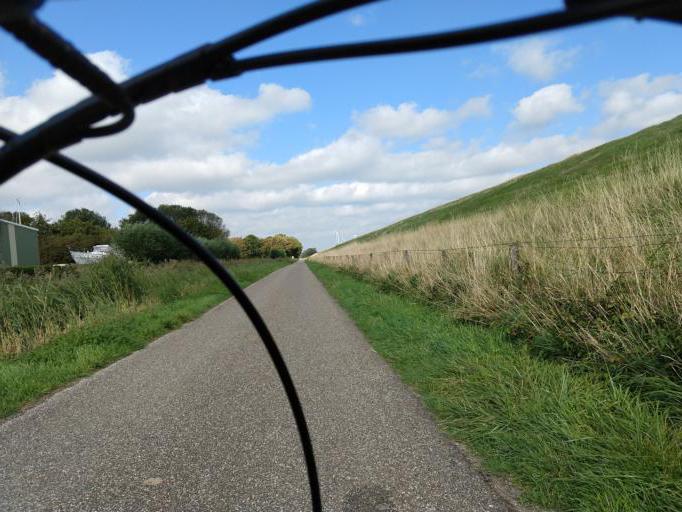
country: NL
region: Zeeland
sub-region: Gemeente Goes
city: Goes
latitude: 51.5750
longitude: 3.8875
